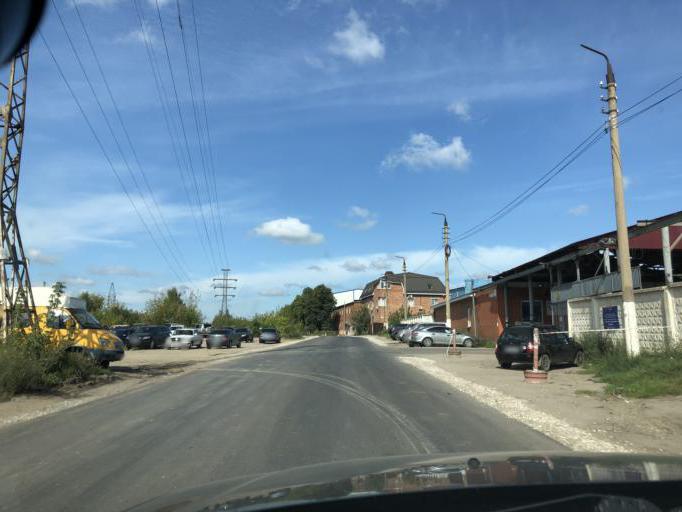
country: RU
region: Tula
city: Tula
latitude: 54.2189
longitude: 37.6741
